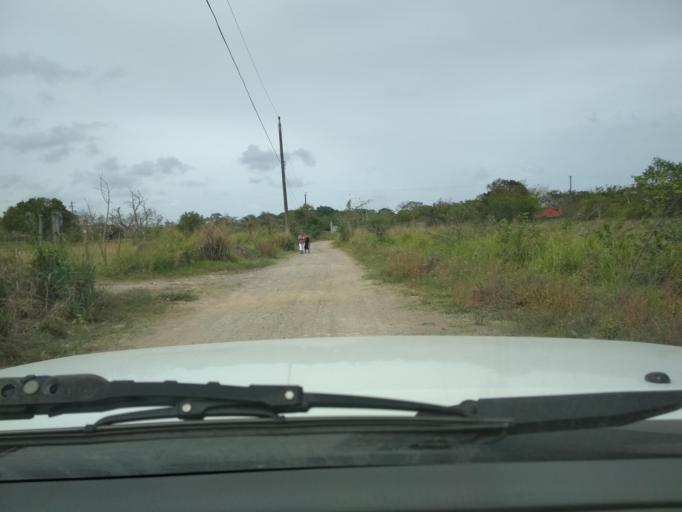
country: MX
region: Veracruz
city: El Tejar
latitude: 19.0648
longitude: -96.1375
